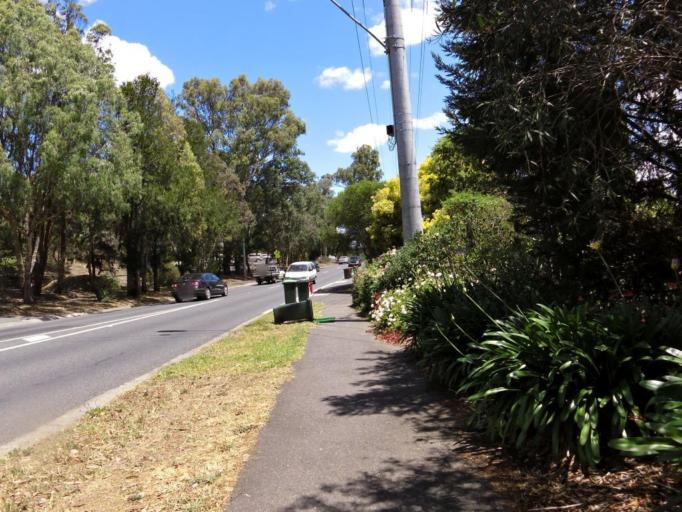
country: AU
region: Victoria
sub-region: Nillumbik
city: Research
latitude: -37.7020
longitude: 145.1853
